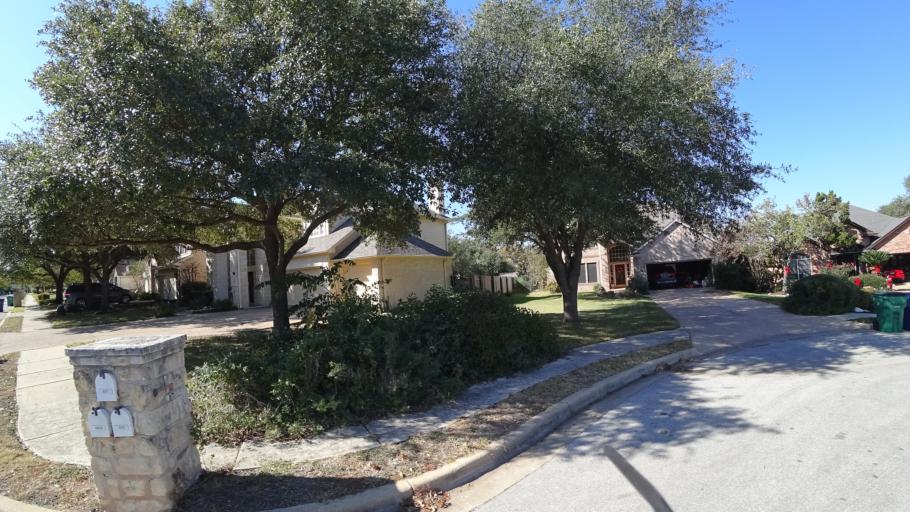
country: US
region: Texas
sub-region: Travis County
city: Lost Creek
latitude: 30.3744
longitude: -97.8421
